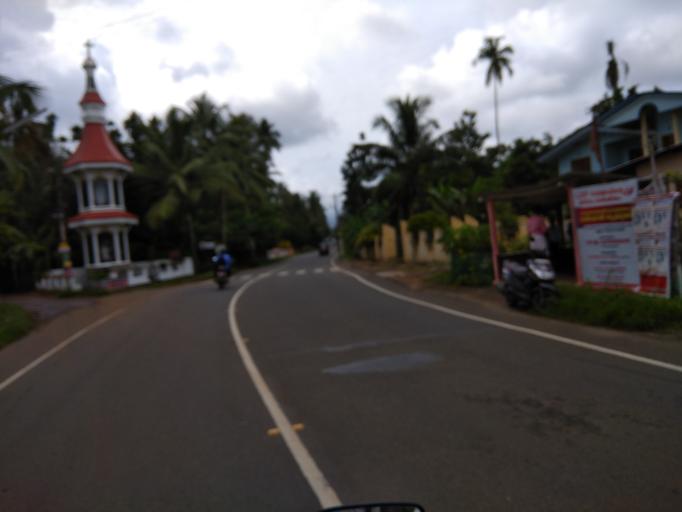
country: IN
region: Kerala
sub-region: Thrissur District
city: Trichur
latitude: 10.5441
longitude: 76.3265
